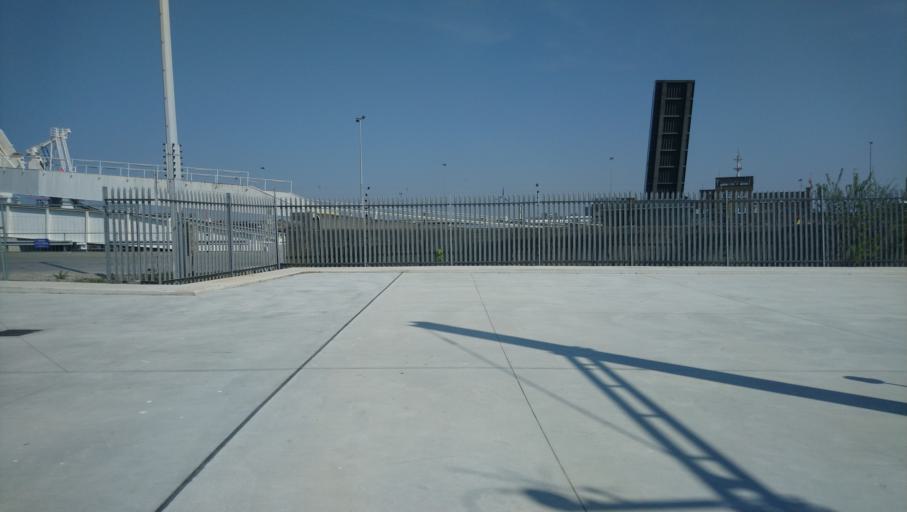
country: BE
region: Flanders
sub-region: Provincie West-Vlaanderen
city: Ostend
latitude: 51.2263
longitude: 2.9283
